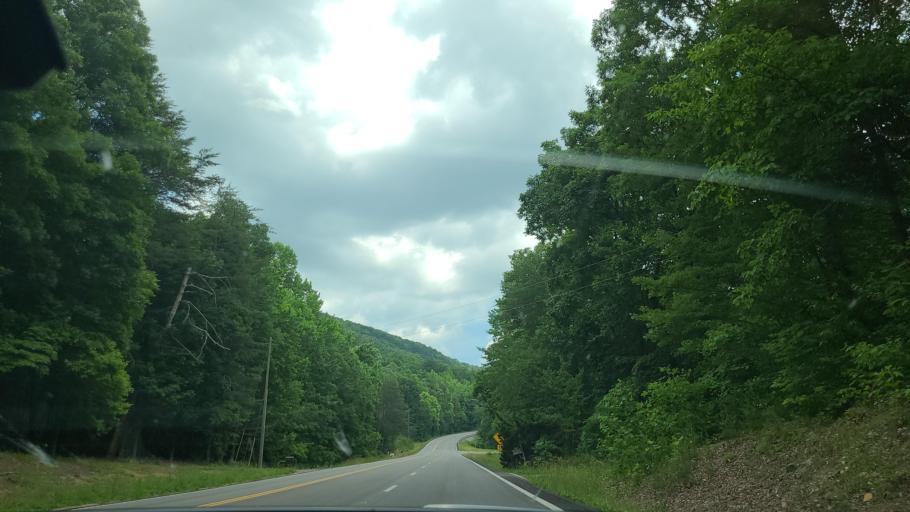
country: US
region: Tennessee
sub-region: Cumberland County
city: Lake Tansi
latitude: 35.7547
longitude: -85.0568
